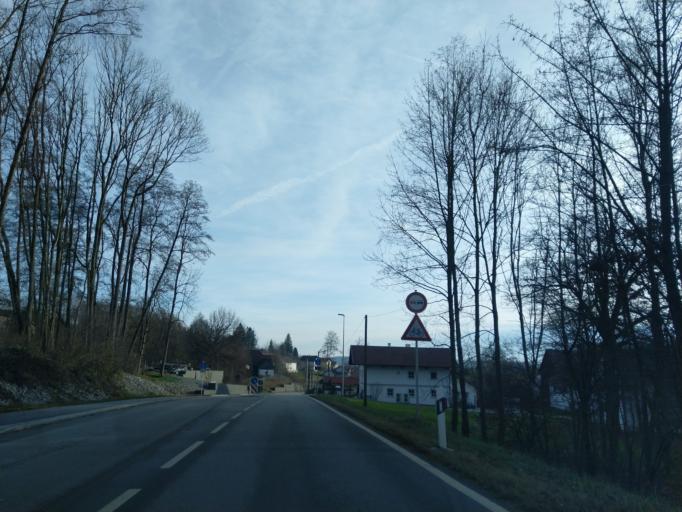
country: DE
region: Bavaria
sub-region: Lower Bavaria
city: Wallerfing
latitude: 48.6584
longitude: 12.8775
